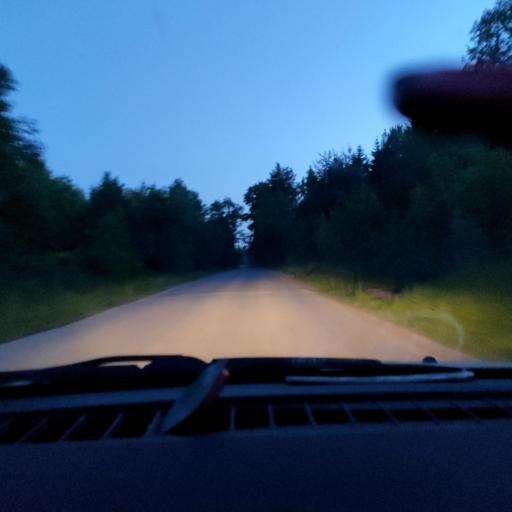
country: RU
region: Perm
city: Kultayevo
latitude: 57.9608
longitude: 55.9165
